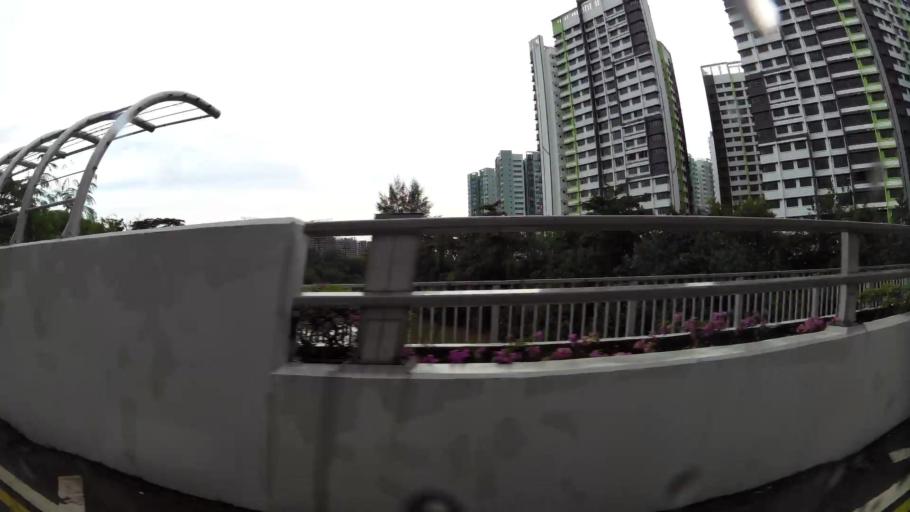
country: MY
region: Johor
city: Kampung Pasir Gudang Baru
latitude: 1.3919
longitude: 103.8814
